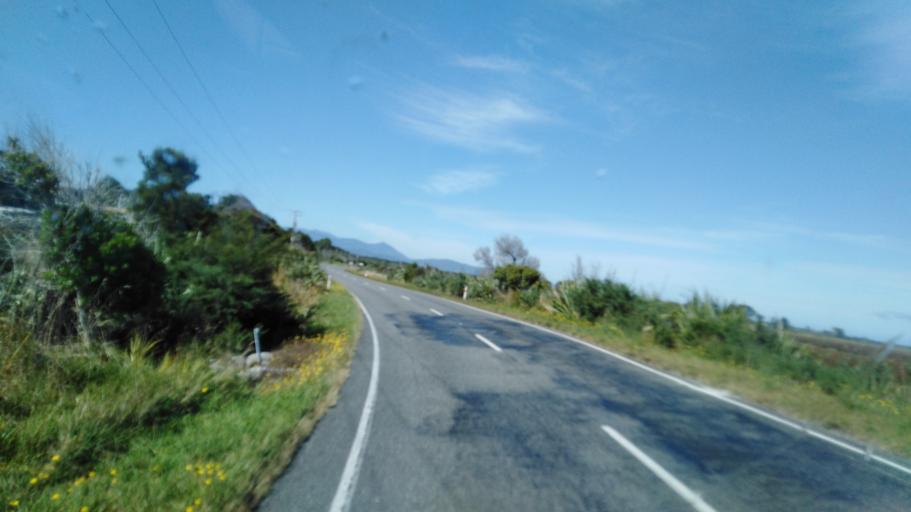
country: NZ
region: West Coast
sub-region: Buller District
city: Westport
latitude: -41.2835
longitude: 172.1044
